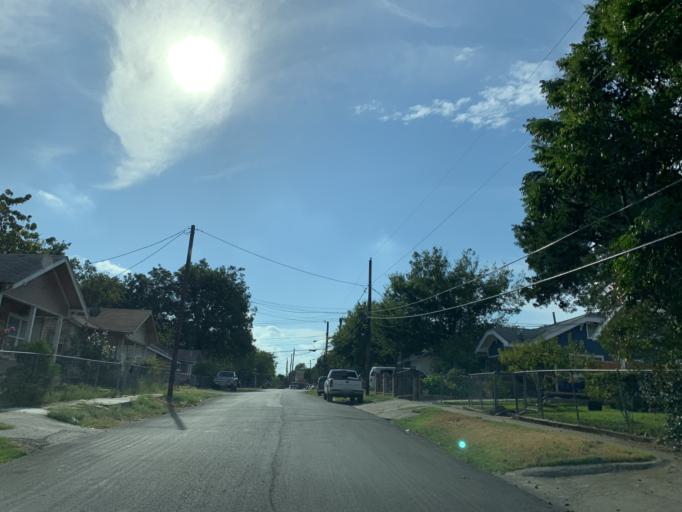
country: US
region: Texas
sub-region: Dallas County
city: Cockrell Hill
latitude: 32.7369
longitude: -96.8352
